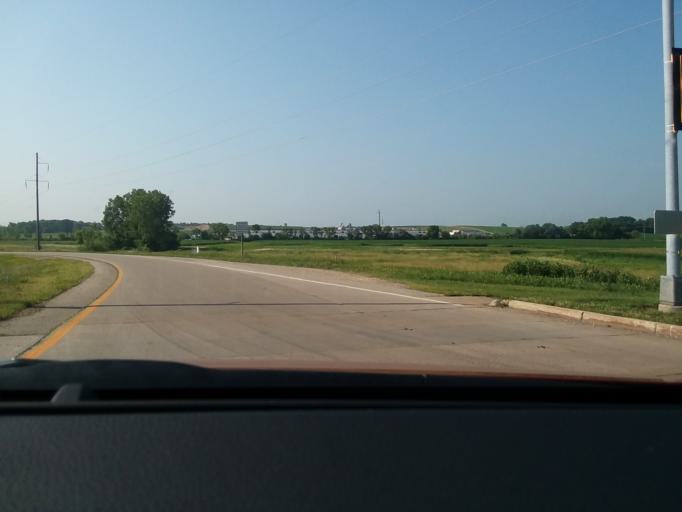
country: US
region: Wisconsin
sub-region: Dane County
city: De Forest
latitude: 43.2504
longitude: -89.3789
